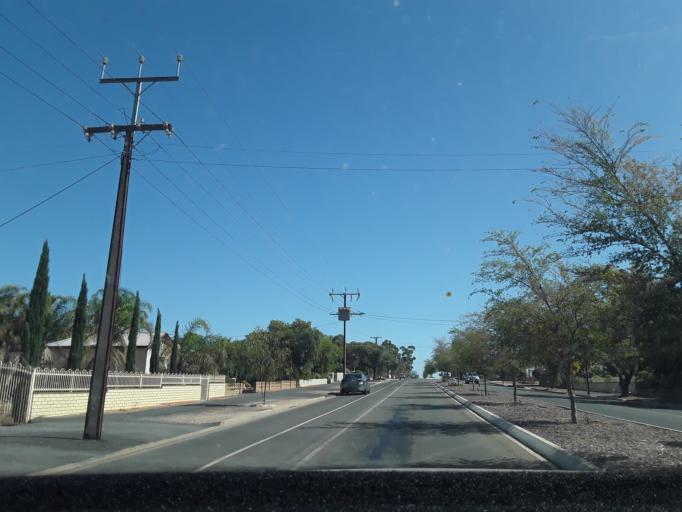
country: AU
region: South Australia
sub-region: Berri and Barmera
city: Barmera
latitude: -34.2563
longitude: 140.4655
